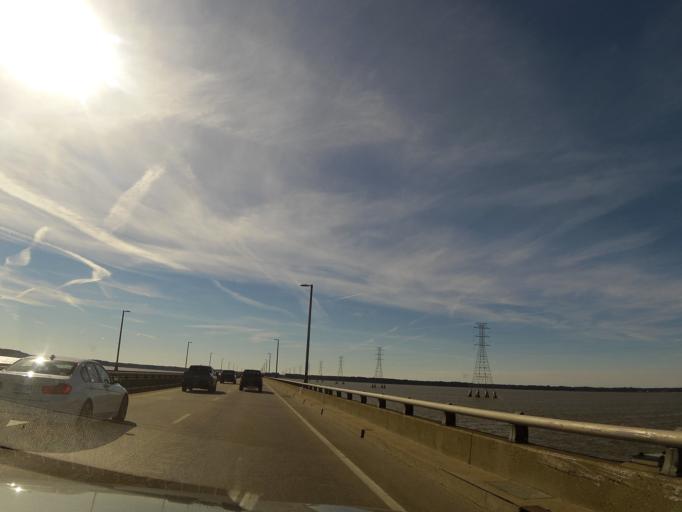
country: US
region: Virginia
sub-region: City of Newport News
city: Newport News
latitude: 36.9857
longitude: -76.4899
